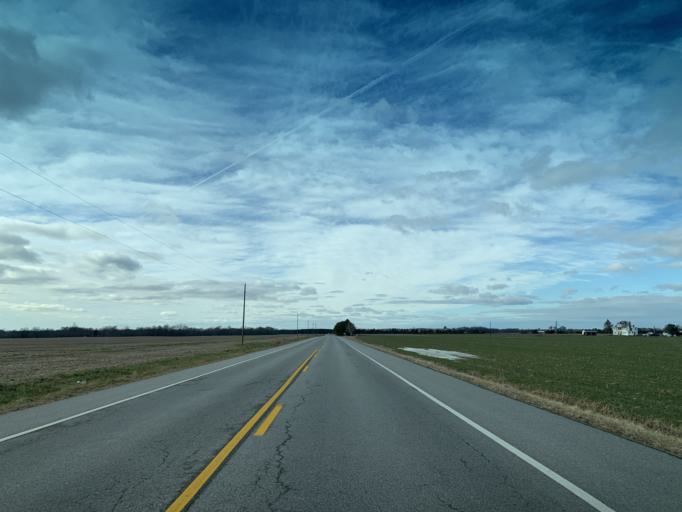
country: US
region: Maryland
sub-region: Queen Anne's County
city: Kingstown
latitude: 39.3235
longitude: -75.9880
